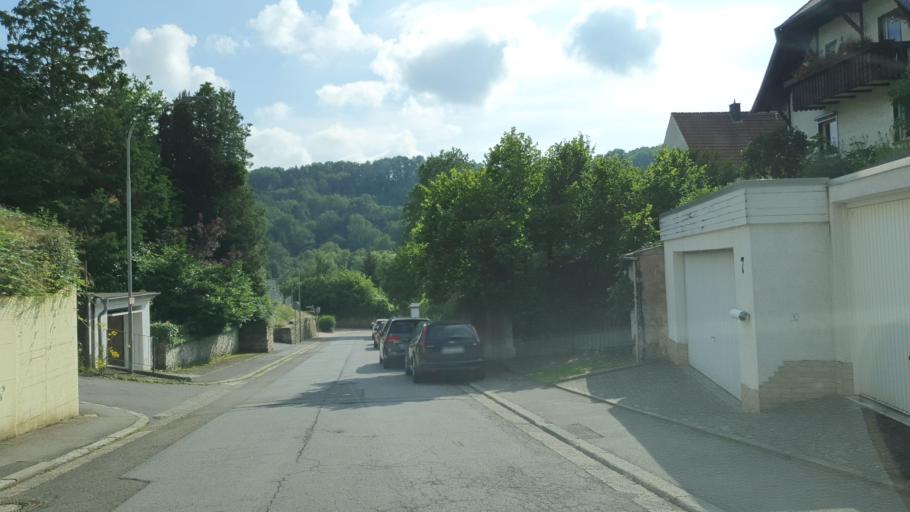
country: DE
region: Saarland
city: Blieskastel
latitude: 49.2518
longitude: 7.2576
